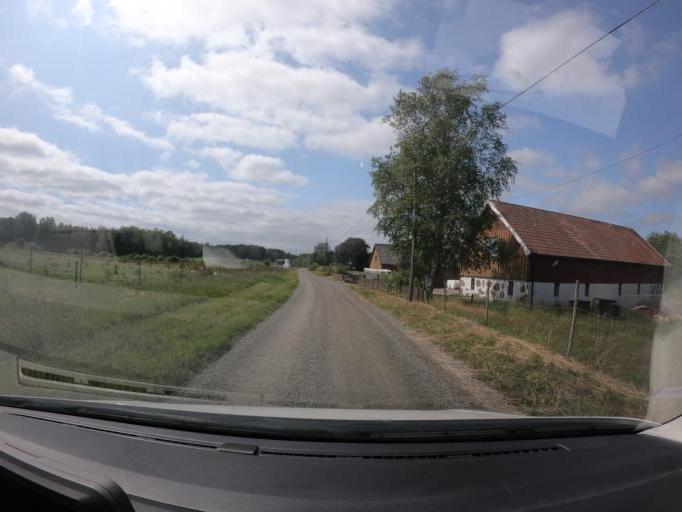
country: SE
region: Skane
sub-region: Hassleholms Kommun
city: Sosdala
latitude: 56.1050
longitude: 13.6579
